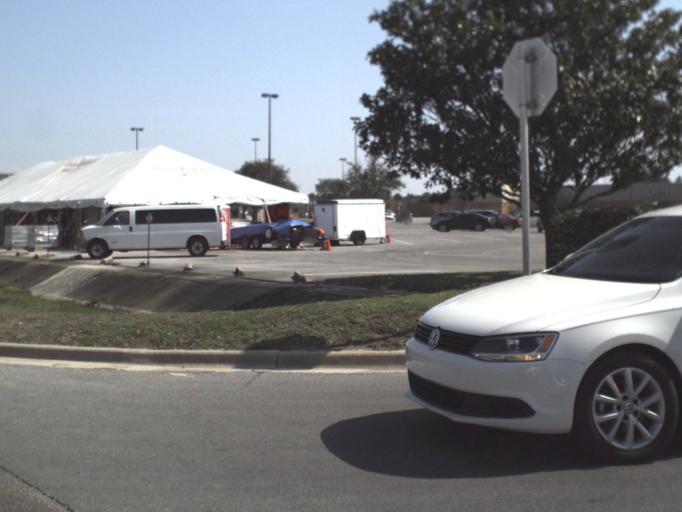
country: US
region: Florida
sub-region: Bay County
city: Hiland Park
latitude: 30.1895
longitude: -85.6476
